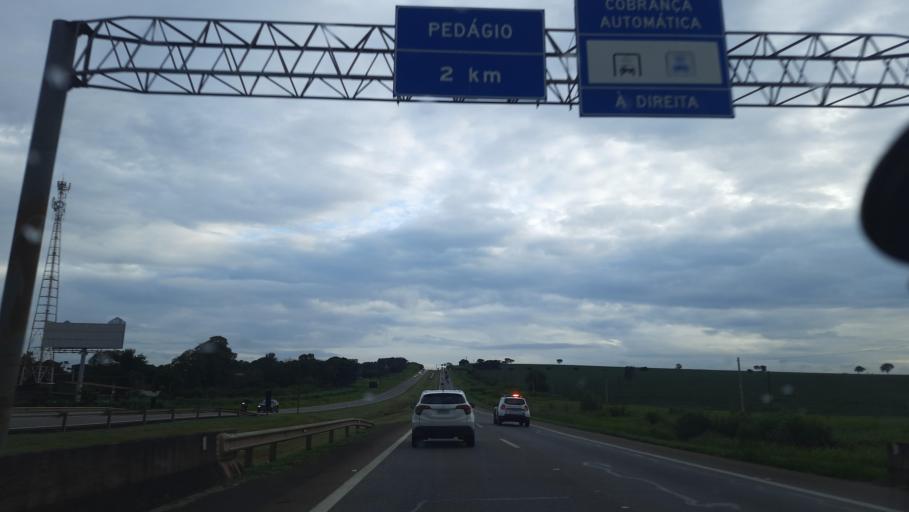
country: BR
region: Sao Paulo
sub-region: Jaguariuna
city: Jaguariuna
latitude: -22.7492
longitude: -47.0203
